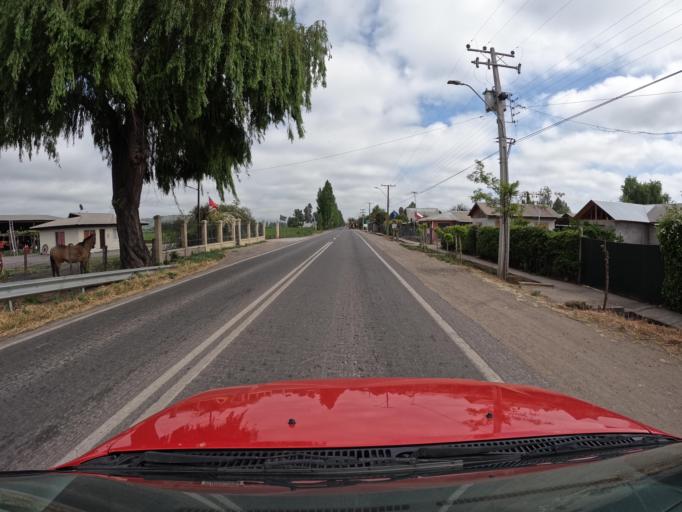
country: CL
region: O'Higgins
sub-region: Provincia de Colchagua
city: Santa Cruz
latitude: -34.6890
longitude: -71.3252
